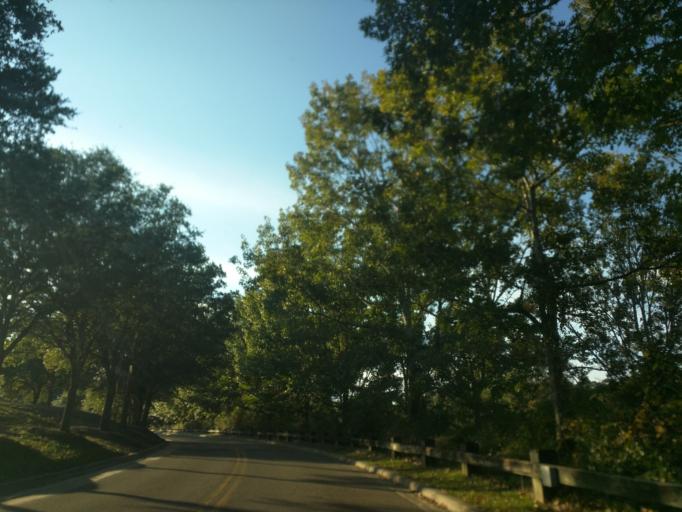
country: US
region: Florida
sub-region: Leon County
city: Tallahassee
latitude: 30.4389
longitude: -84.2535
